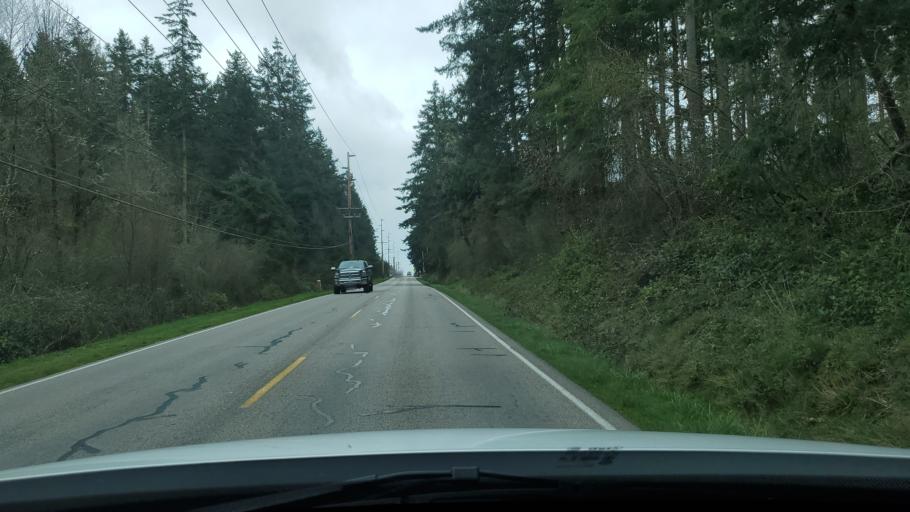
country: US
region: Washington
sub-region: Island County
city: Oak Harbor
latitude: 48.3062
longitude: -122.6321
